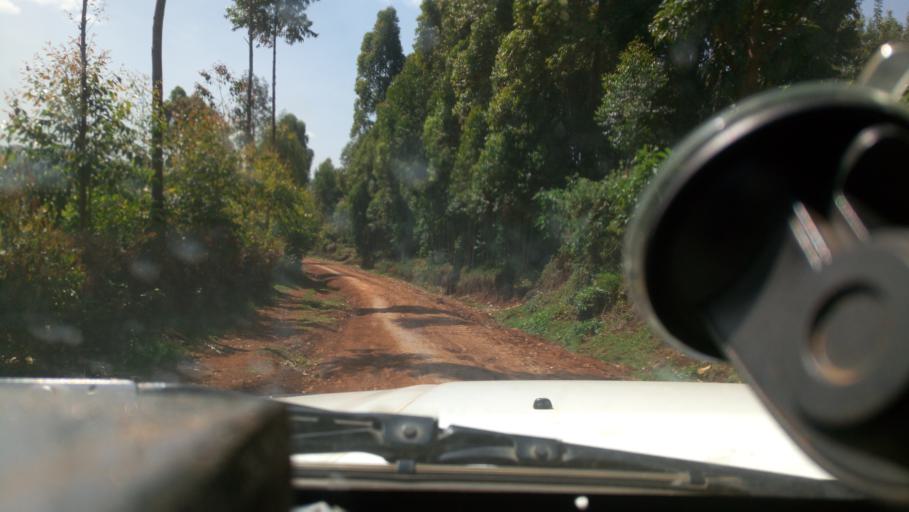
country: KE
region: Nyamira District
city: Nyamira
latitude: -0.6173
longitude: 34.8992
